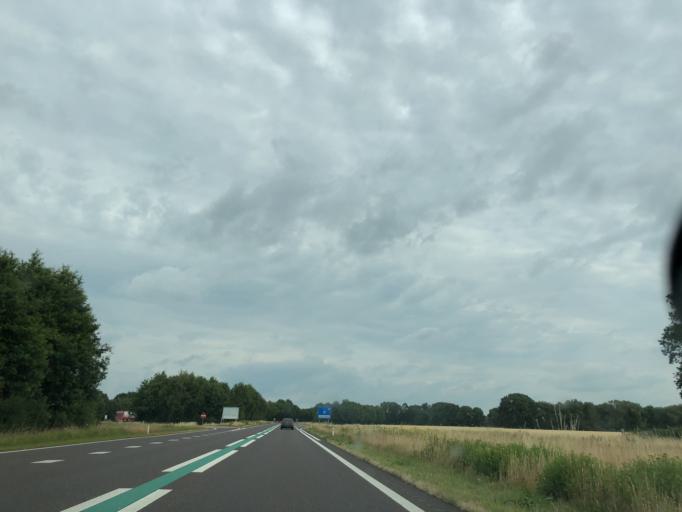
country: NL
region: Drenthe
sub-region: Gemeente Aa en Hunze
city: Anloo
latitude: 53.0280
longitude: 6.7399
